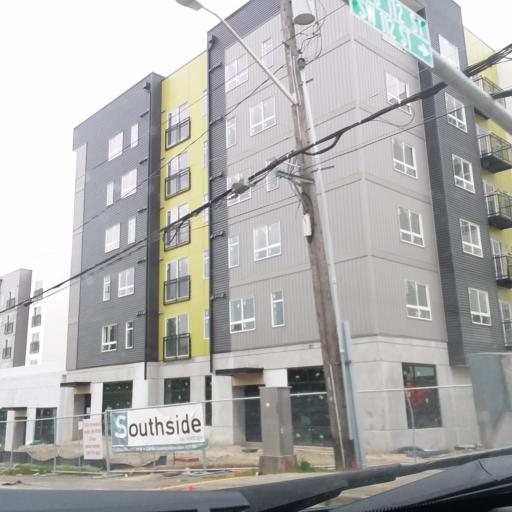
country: US
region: Washington
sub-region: King County
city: Boulevard Park
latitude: 47.5031
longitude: -122.3337
